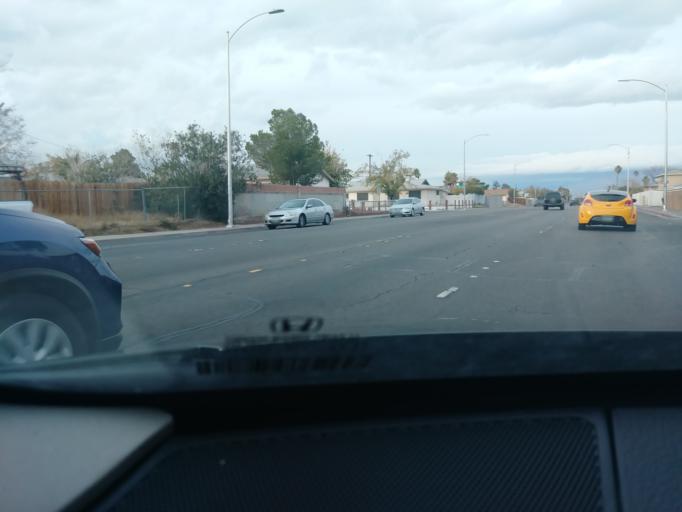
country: US
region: Nevada
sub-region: Clark County
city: Spring Valley
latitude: 36.1766
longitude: -115.2240
